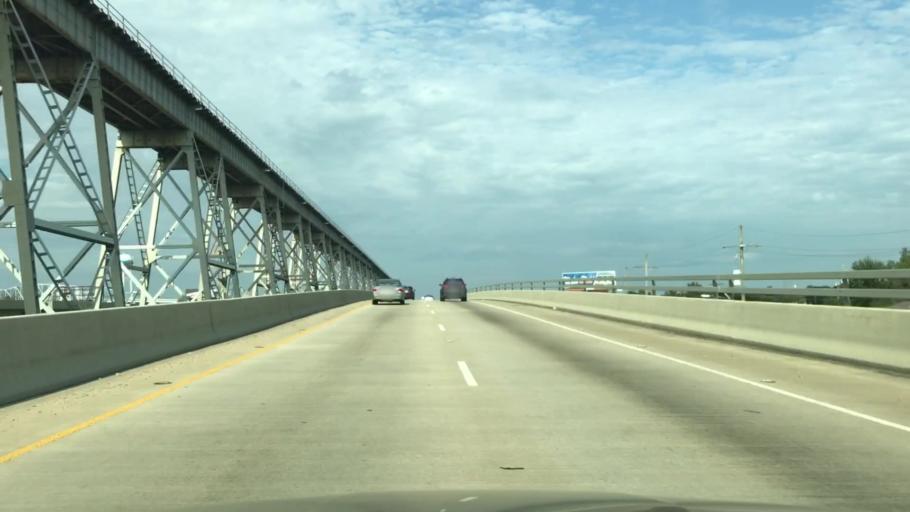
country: US
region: Louisiana
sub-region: Jefferson Parish
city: Bridge City
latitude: 29.9287
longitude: -90.1658
